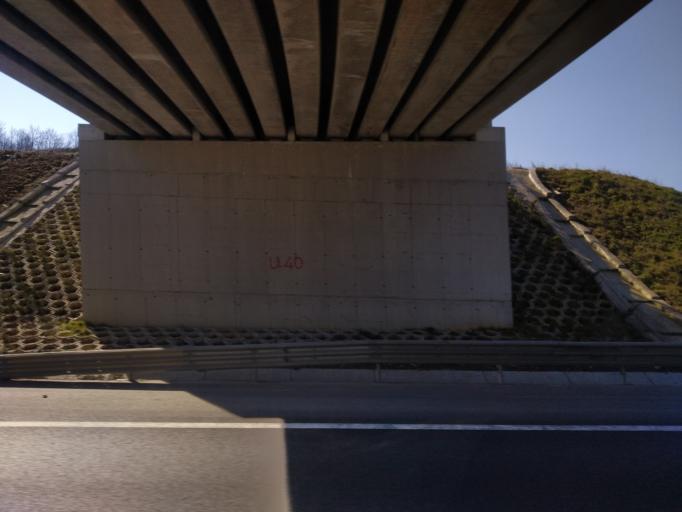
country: TR
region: Istanbul
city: Mahmut Sevket Pasa
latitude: 41.1623
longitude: 29.2578
